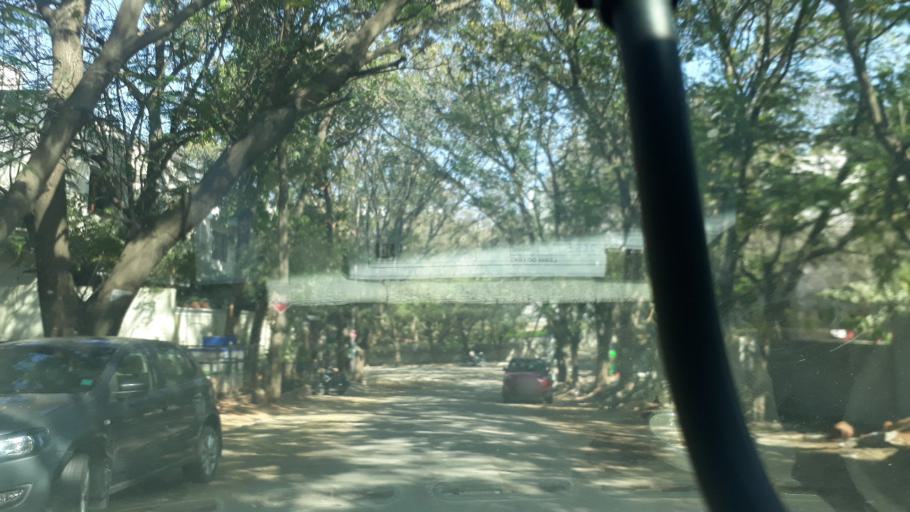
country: IN
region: Telangana
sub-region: Rangareddi
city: Kukatpalli
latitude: 17.4232
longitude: 78.4014
